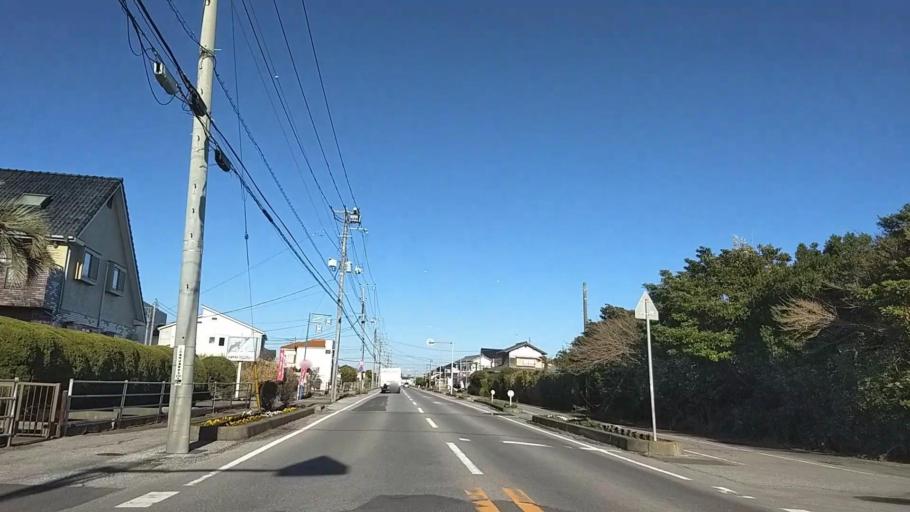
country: JP
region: Chiba
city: Togane
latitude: 35.5105
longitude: 140.4355
